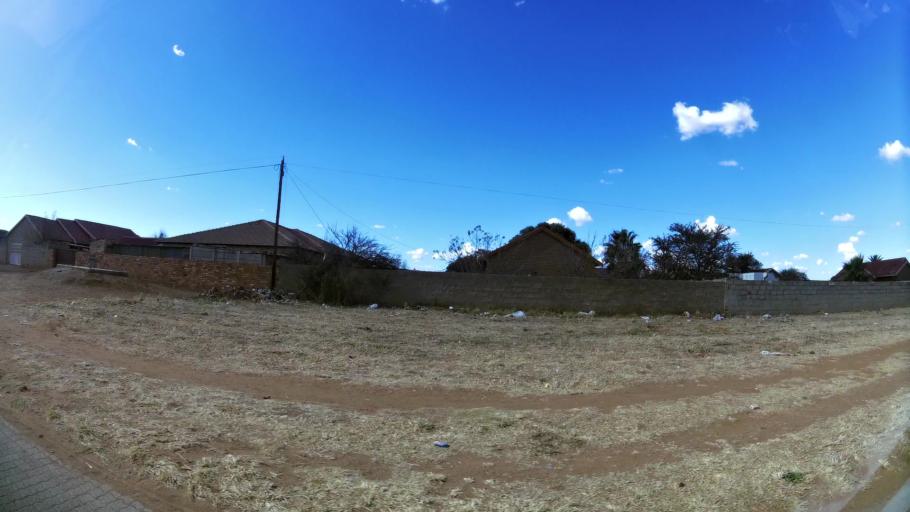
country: ZA
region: North-West
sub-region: Dr Kenneth Kaunda District Municipality
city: Klerksdorp
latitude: -26.8756
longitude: 26.5822
